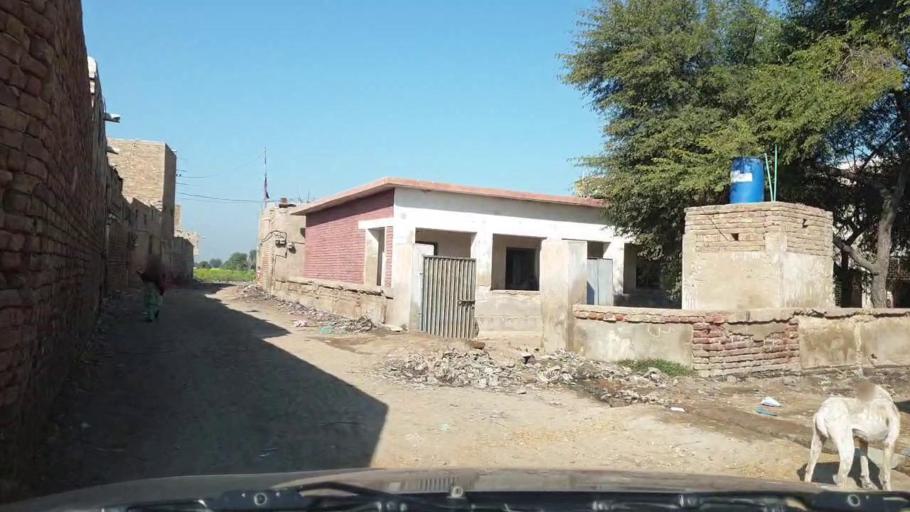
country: PK
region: Sindh
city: Jhol
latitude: 25.9433
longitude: 68.8198
